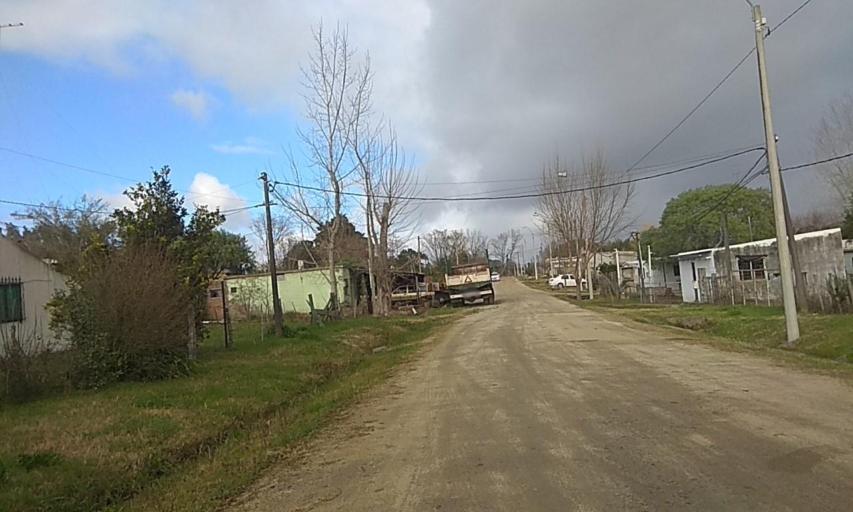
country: UY
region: Florida
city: Florida
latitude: -34.0904
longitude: -56.1990
